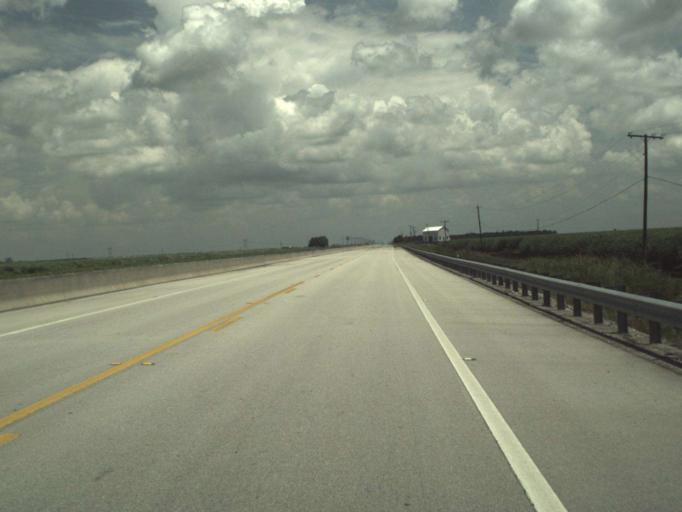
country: US
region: Florida
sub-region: Palm Beach County
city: Pahokee
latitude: 26.8454
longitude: -80.6063
